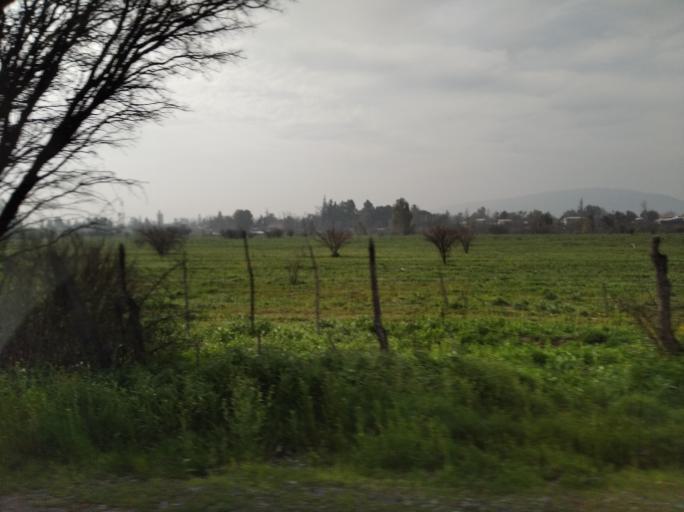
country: CL
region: Santiago Metropolitan
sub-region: Provincia de Chacabuco
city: Lampa
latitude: -33.1696
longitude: -70.8944
